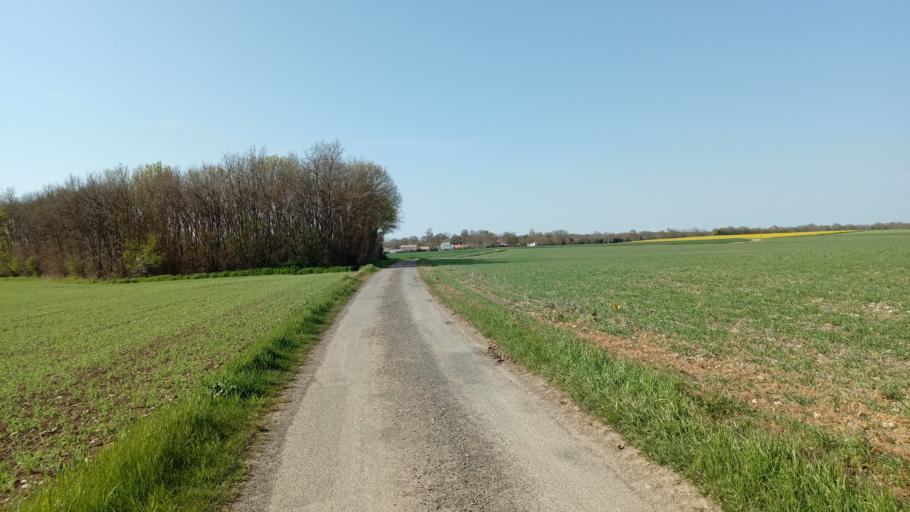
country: FR
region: Poitou-Charentes
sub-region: Departement de la Charente-Maritime
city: Verines
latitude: 46.1625
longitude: -0.9398
